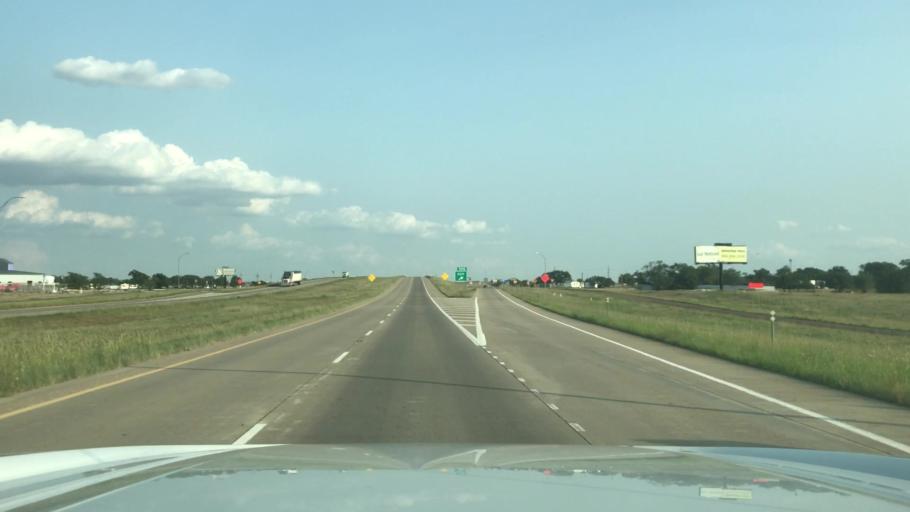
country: US
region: Texas
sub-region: Randall County
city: Canyon
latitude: 34.9838
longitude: -101.8840
